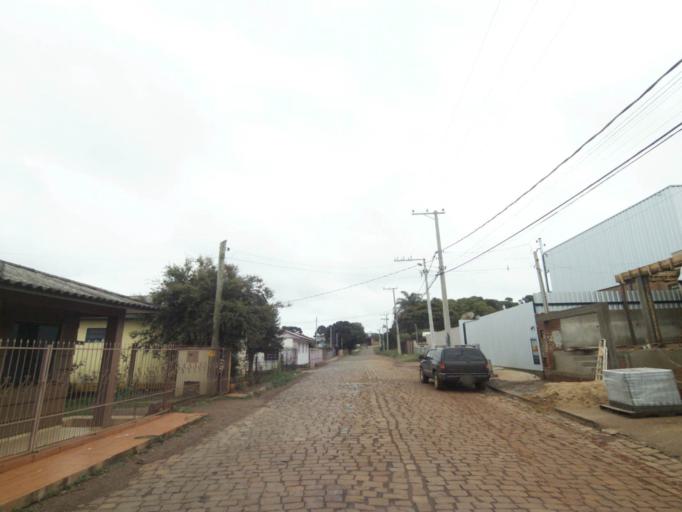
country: BR
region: Rio Grande do Sul
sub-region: Lagoa Vermelha
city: Lagoa Vermelha
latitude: -28.2210
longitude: -51.5210
